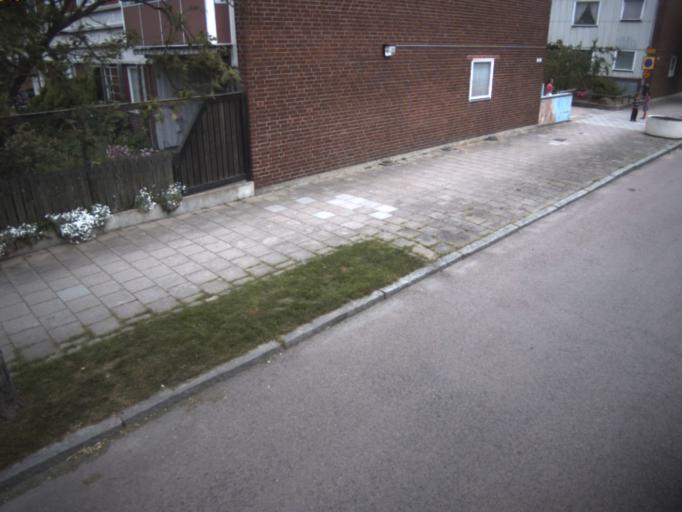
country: SE
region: Skane
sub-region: Helsingborg
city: Helsingborg
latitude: 56.0630
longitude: 12.7188
